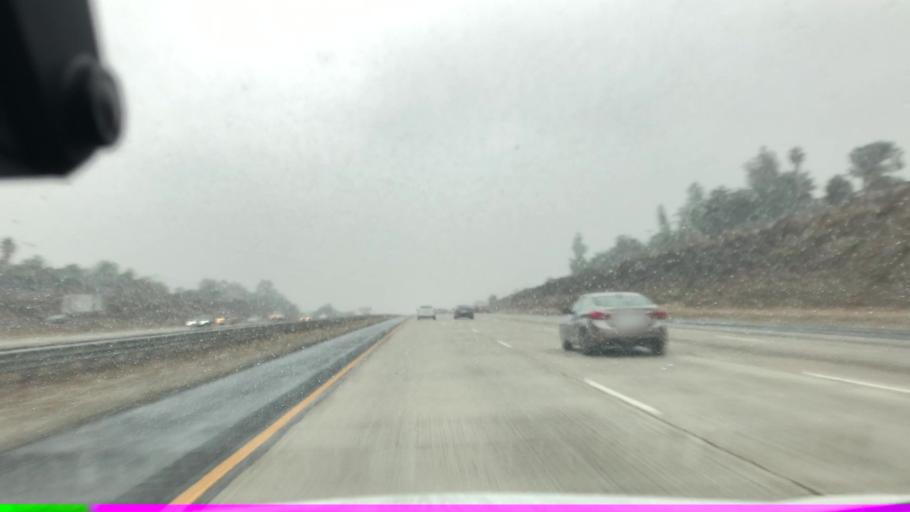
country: US
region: California
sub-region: San Diego County
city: Hidden Meadows
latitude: 33.1898
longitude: -117.1215
